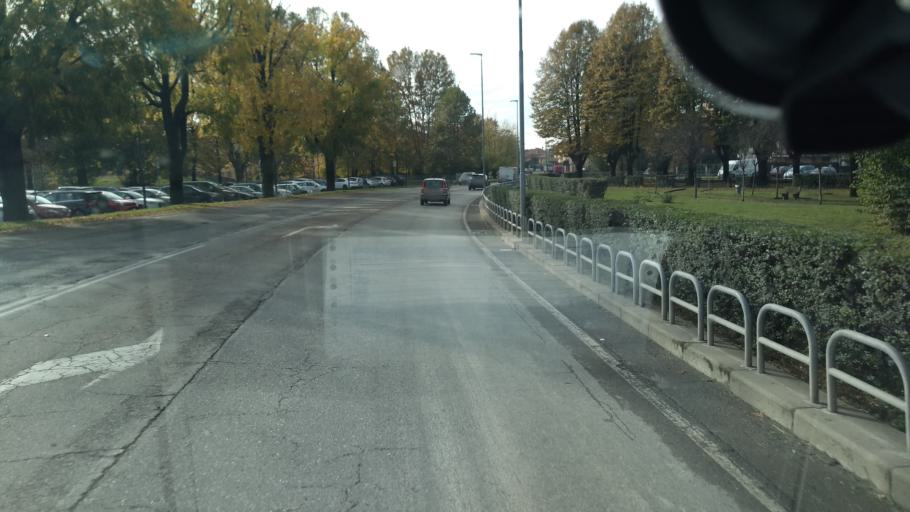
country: IT
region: Lombardy
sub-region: Provincia di Bergamo
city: Cologno al Serio
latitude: 45.5815
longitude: 9.7054
